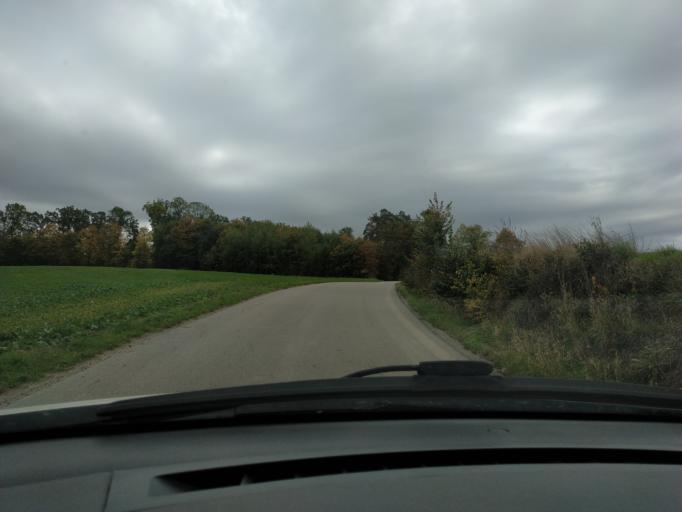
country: PL
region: Warmian-Masurian Voivodeship
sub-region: Powiat nowomiejski
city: Biskupiec
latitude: 53.4557
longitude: 19.3155
